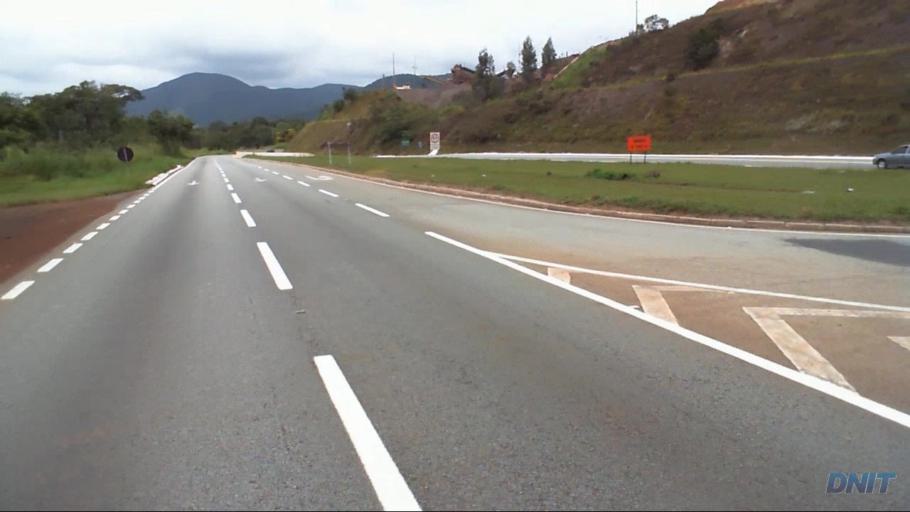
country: BR
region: Minas Gerais
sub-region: Caete
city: Caete
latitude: -19.7867
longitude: -43.6851
